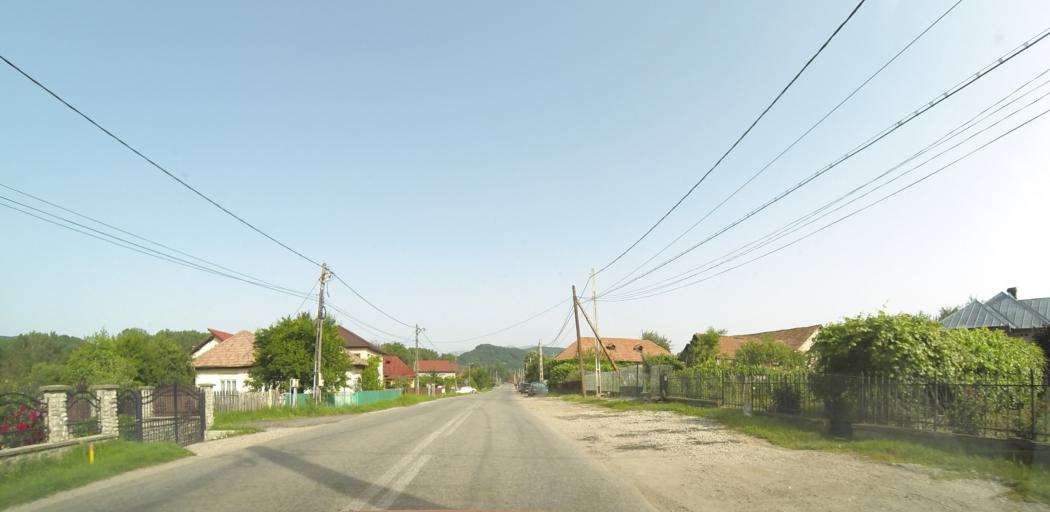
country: RO
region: Valcea
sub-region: Comuna Pausesti-Maglasi
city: Pausesti-Maglasi
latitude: 45.1330
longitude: 24.2567
